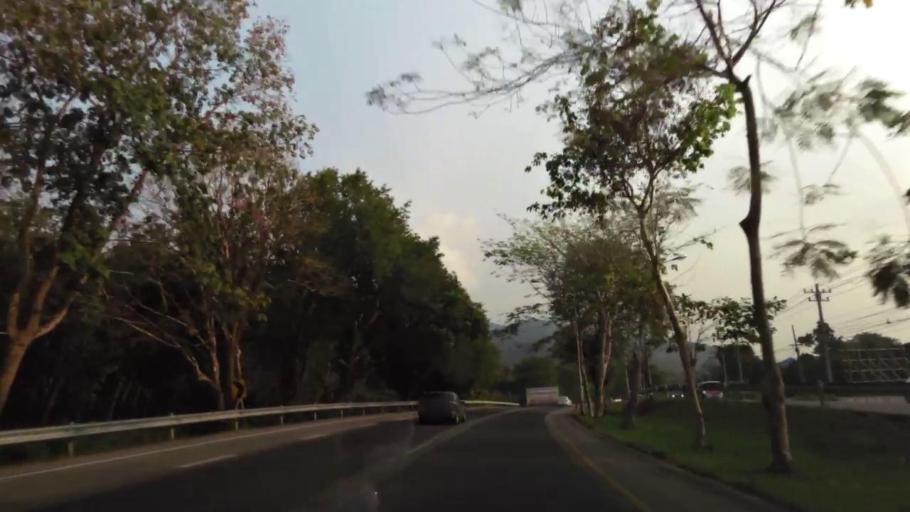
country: TH
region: Chanthaburi
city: Chanthaburi
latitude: 12.5749
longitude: 102.1617
